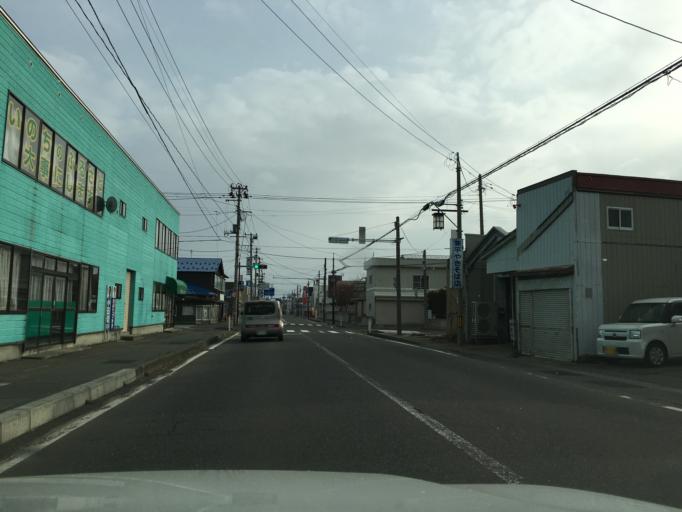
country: JP
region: Aomori
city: Namioka
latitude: 40.7133
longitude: 140.5906
